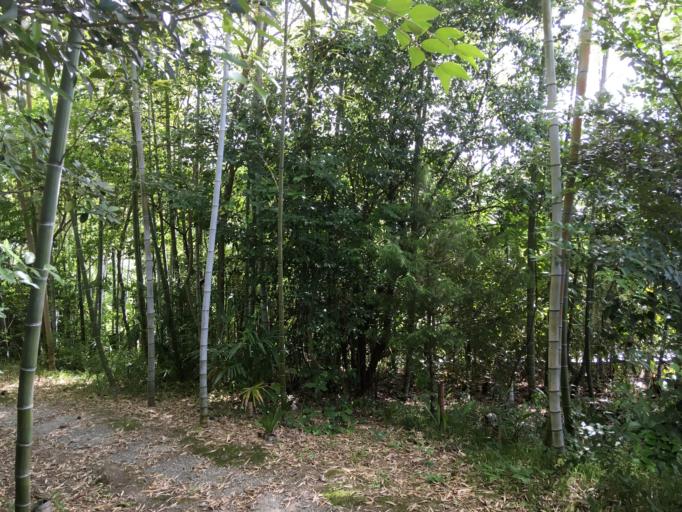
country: JP
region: Nara
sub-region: Ikoma-shi
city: Ikoma
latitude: 34.7104
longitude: 135.7469
